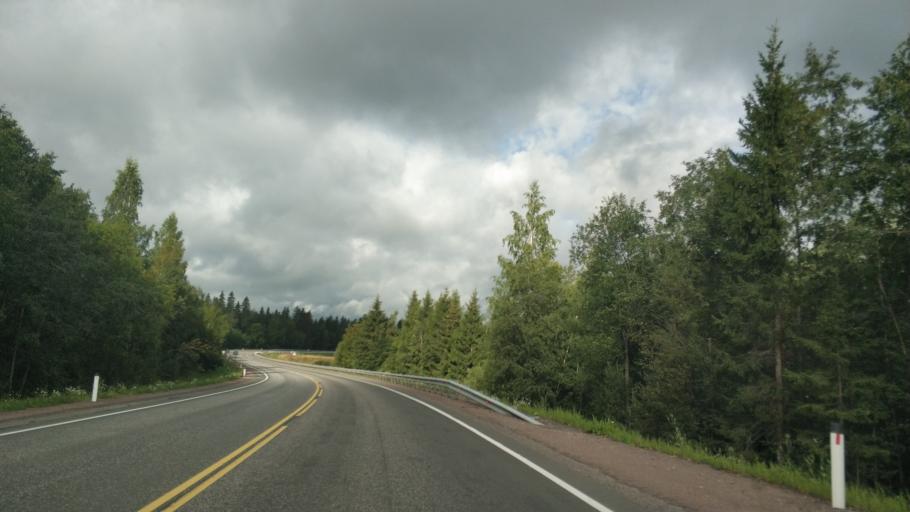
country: RU
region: Republic of Karelia
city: Khelyulya
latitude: 61.7851
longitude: 30.6506
